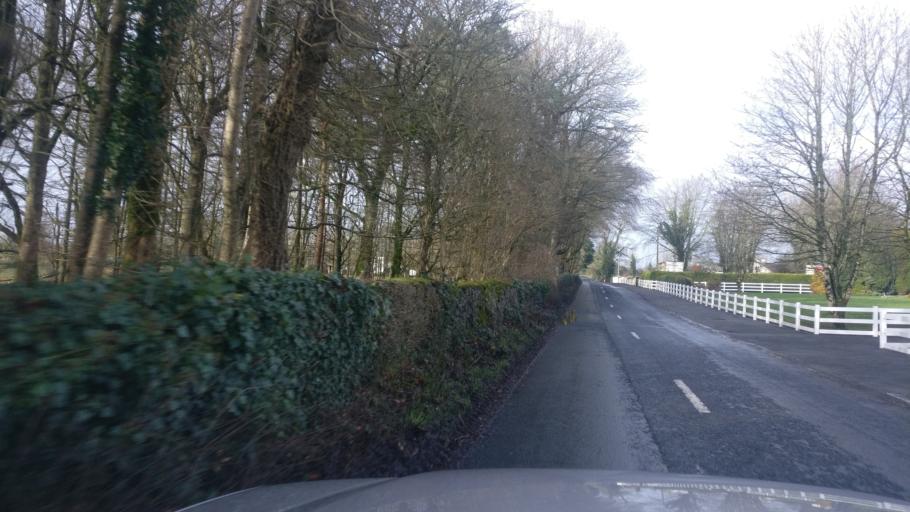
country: IE
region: Connaught
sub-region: County Galway
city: Loughrea
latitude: 53.2849
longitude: -8.5915
